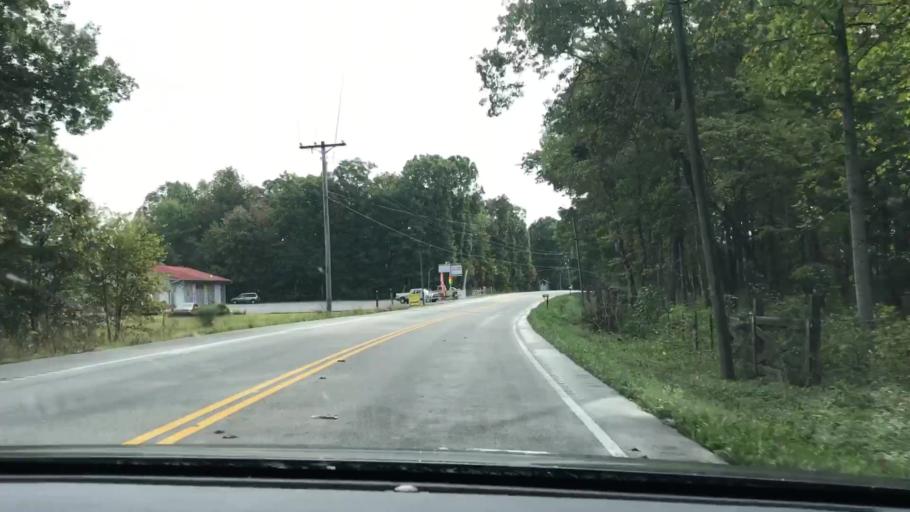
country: US
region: Tennessee
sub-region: Fentress County
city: Jamestown
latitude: 36.3723
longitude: -84.8567
